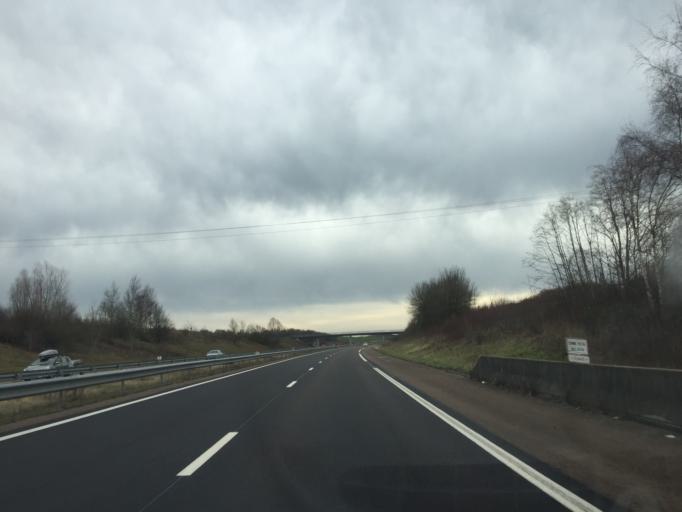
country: FR
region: Franche-Comte
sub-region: Departement du Jura
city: Bletterans
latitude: 46.7456
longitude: 5.5108
